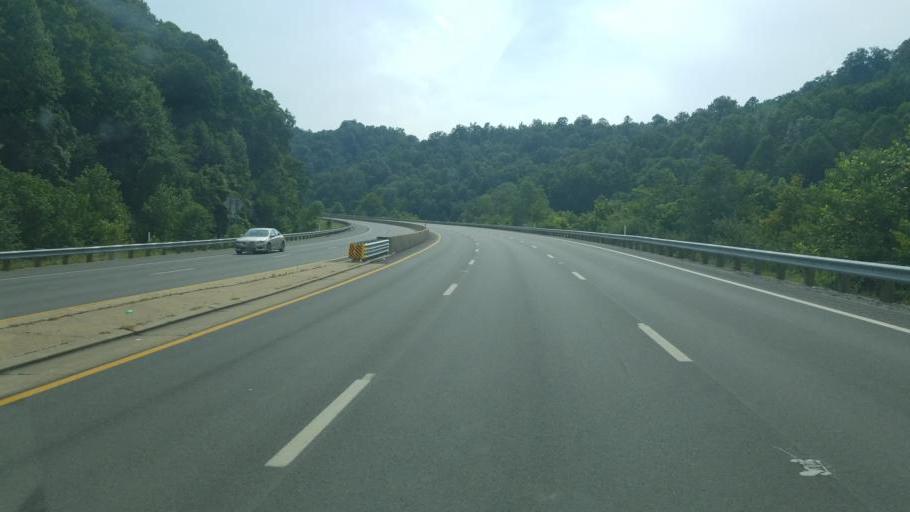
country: US
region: West Virginia
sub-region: Logan County
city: Chapmanville
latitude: 37.9270
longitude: -82.0271
